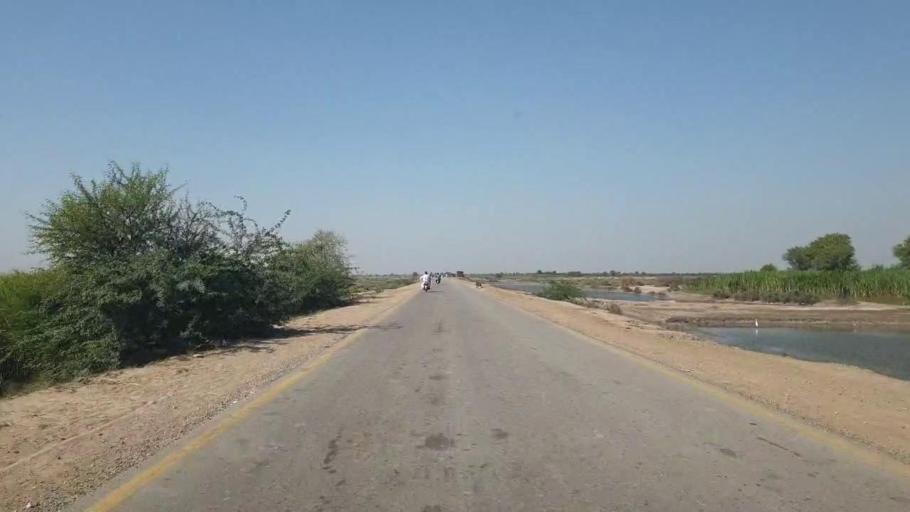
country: PK
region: Sindh
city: Rajo Khanani
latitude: 25.0129
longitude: 68.8324
